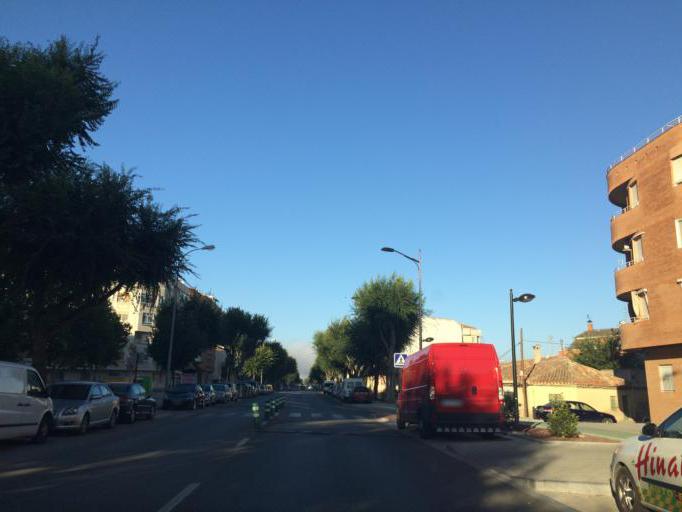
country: ES
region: Castille-La Mancha
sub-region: Provincia de Albacete
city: Albacete
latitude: 39.0032
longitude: -1.8671
